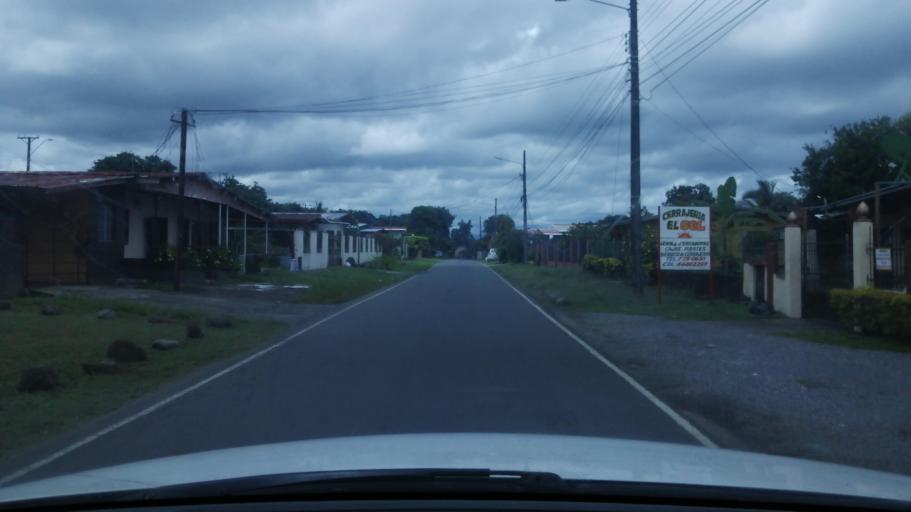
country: PA
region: Chiriqui
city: David
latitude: 8.4300
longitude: -82.4188
